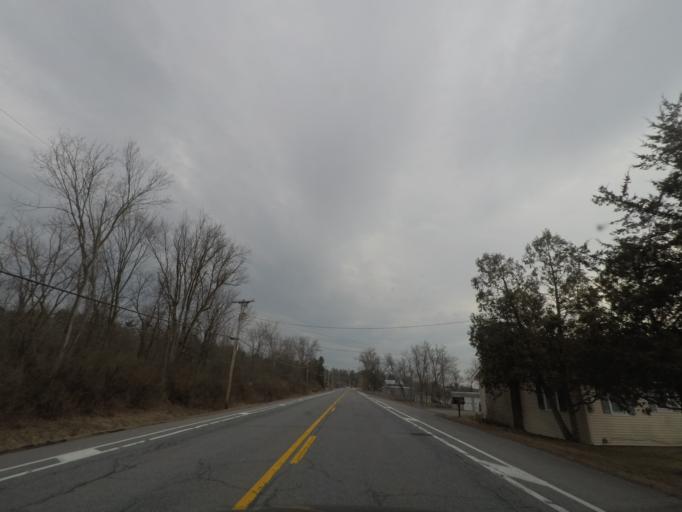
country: US
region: New York
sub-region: Washington County
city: Fort Edward
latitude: 43.2115
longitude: -73.5773
